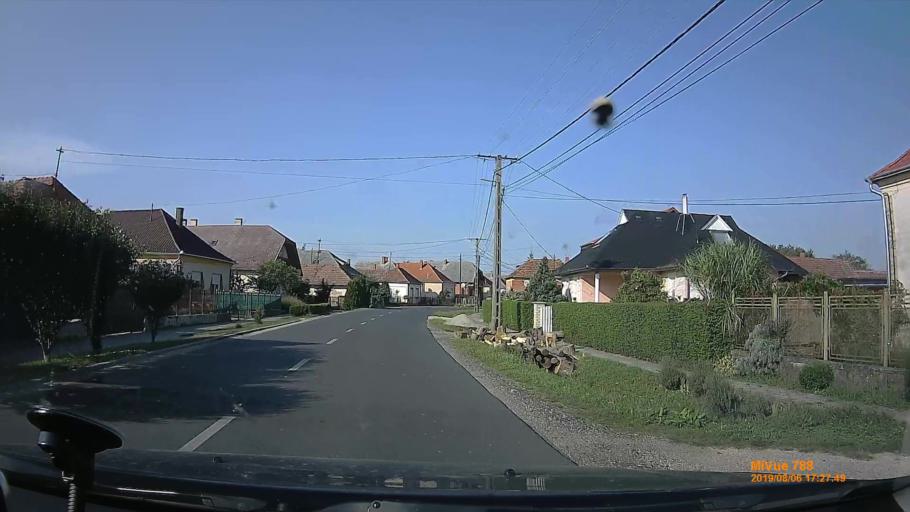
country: HR
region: Medimurska
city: Kotoriba
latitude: 46.3880
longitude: 16.8348
